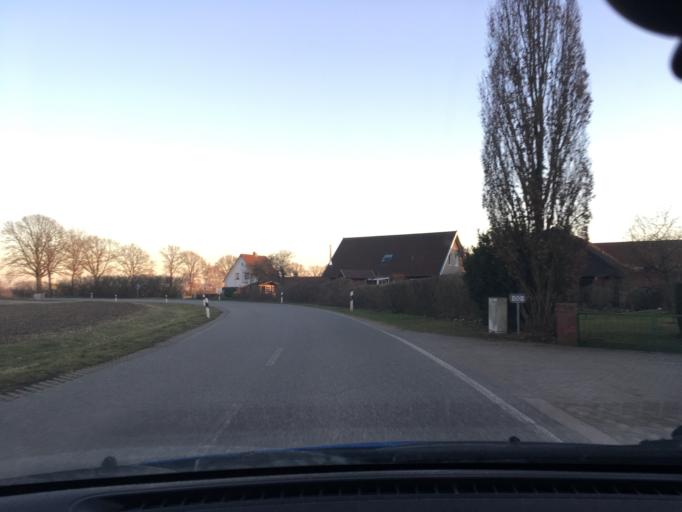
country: DE
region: Schleswig-Holstein
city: Fitzen
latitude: 53.4804
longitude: 10.6406
